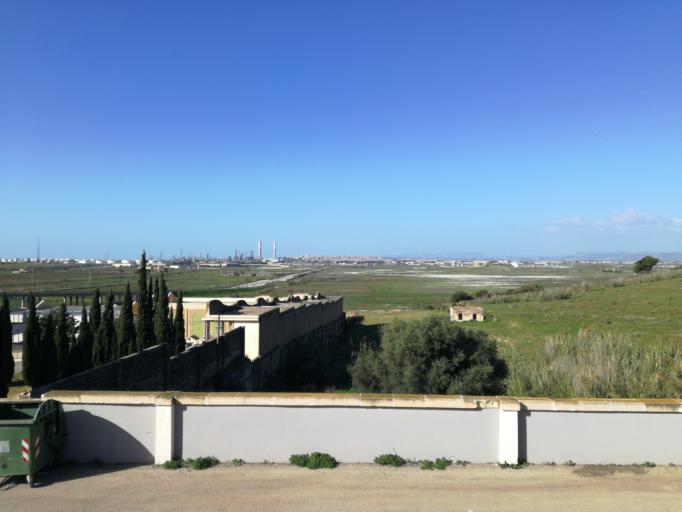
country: IT
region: Sicily
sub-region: Provincia di Caltanissetta
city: Gela
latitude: 37.0578
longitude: 14.3167
